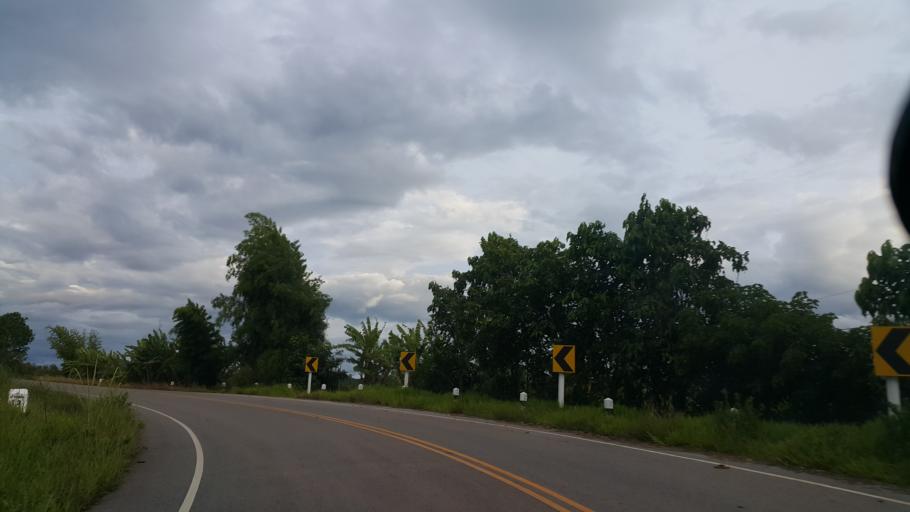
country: TH
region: Loei
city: Na Haeo
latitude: 17.4714
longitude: 101.1153
